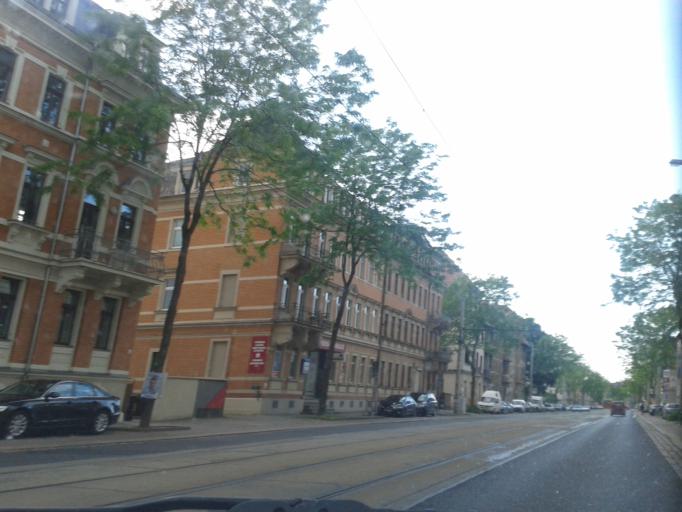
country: DE
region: Saxony
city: Dresden
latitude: 51.0864
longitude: 13.7262
